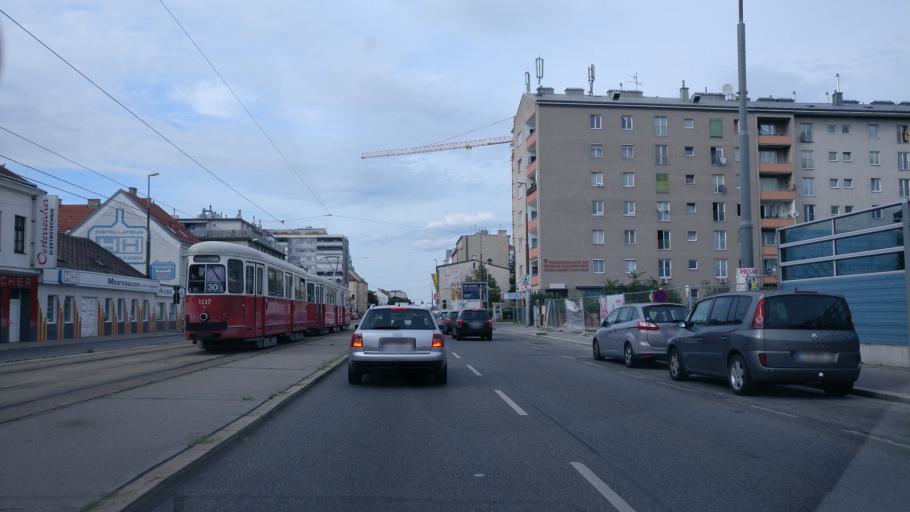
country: AT
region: Lower Austria
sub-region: Politischer Bezirk Korneuburg
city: Hagenbrunn
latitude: 48.2742
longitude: 16.4074
